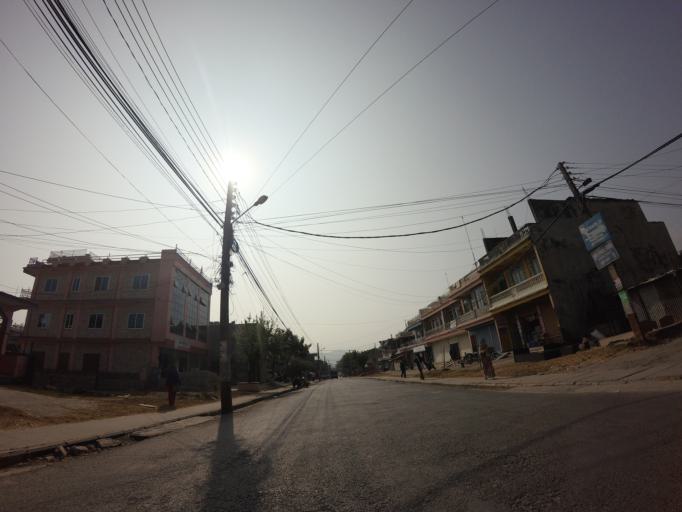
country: NP
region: Western Region
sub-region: Gandaki Zone
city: Pokhara
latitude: 28.2181
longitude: 83.9837
